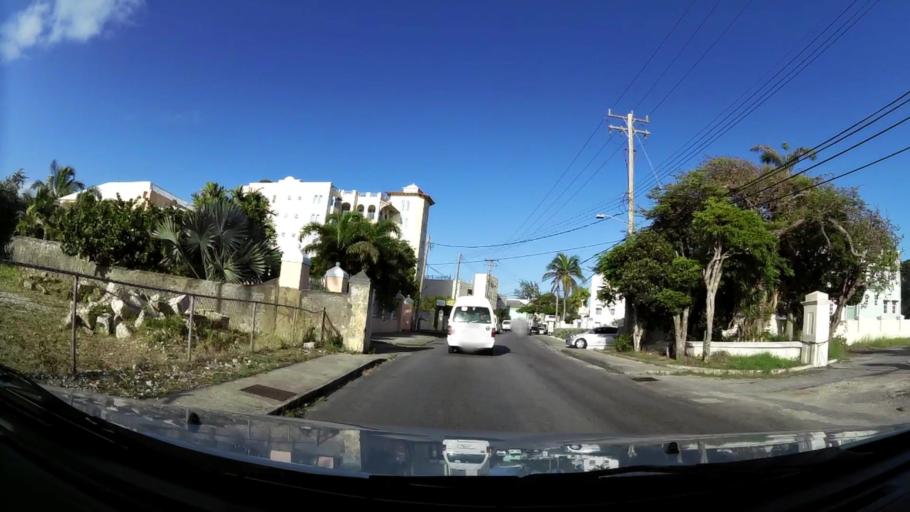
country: BB
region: Saint Michael
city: Bridgetown
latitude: 13.0744
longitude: -59.5987
